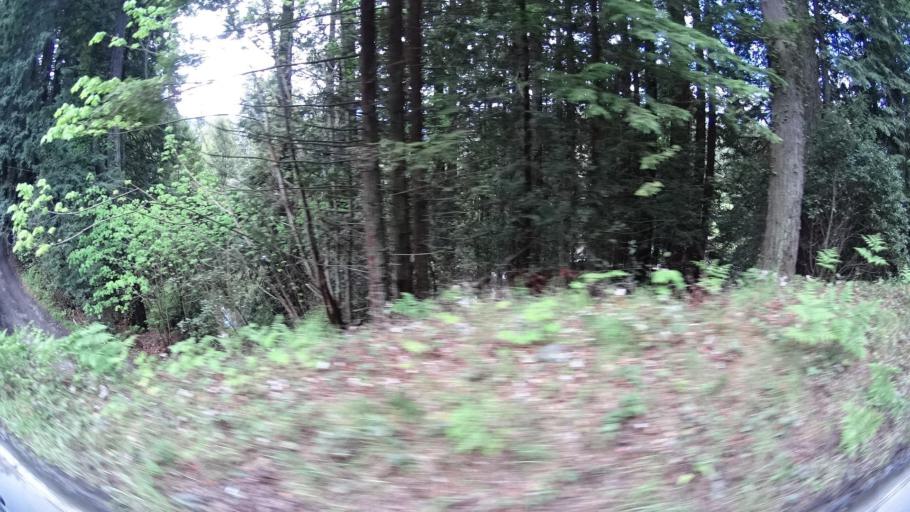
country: US
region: California
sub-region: Humboldt County
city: Blue Lake
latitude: 40.8724
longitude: -123.9759
